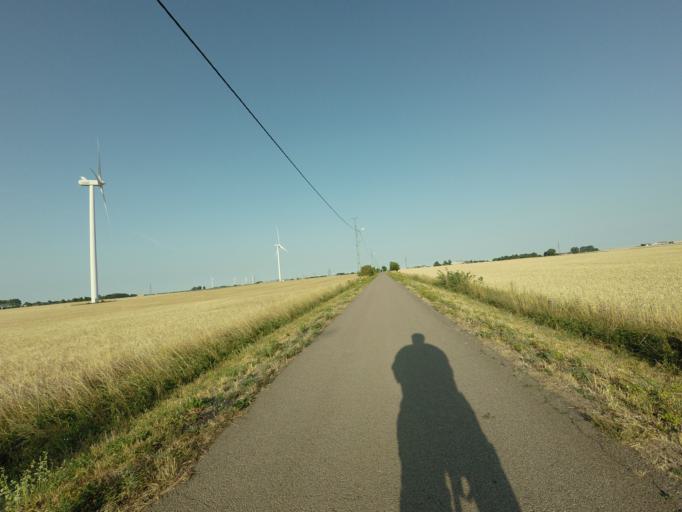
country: SE
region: Skane
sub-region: Landskrona
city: Asmundtorp
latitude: 55.8787
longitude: 12.9057
